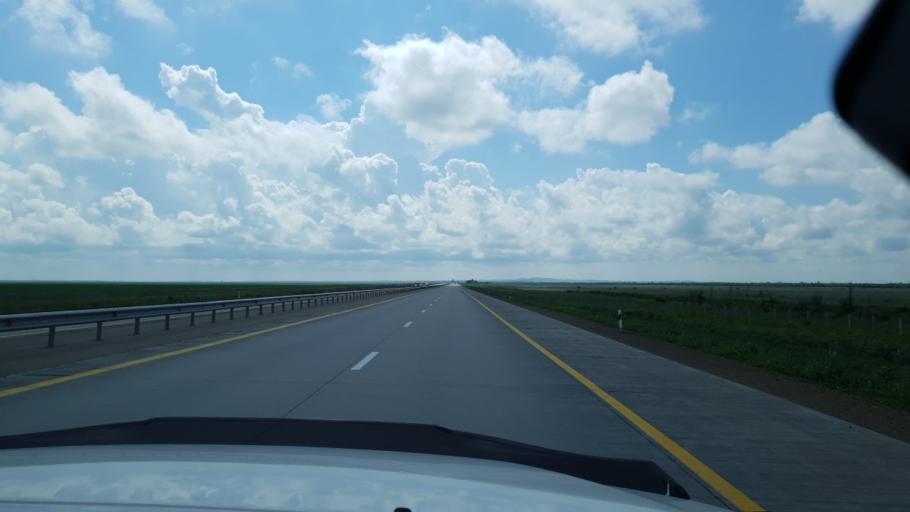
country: KZ
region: Qaraghandy
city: Osakarovka
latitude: 50.7188
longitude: 72.3183
